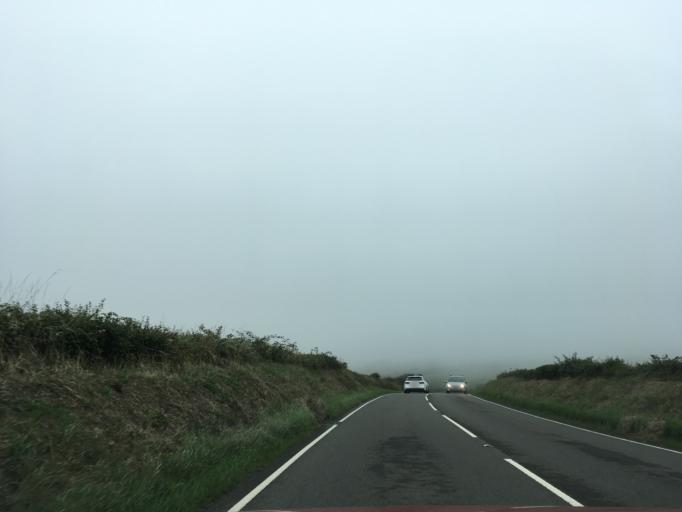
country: GB
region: Wales
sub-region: Pembrokeshire
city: Llanrhian
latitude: 51.8757
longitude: -5.1674
